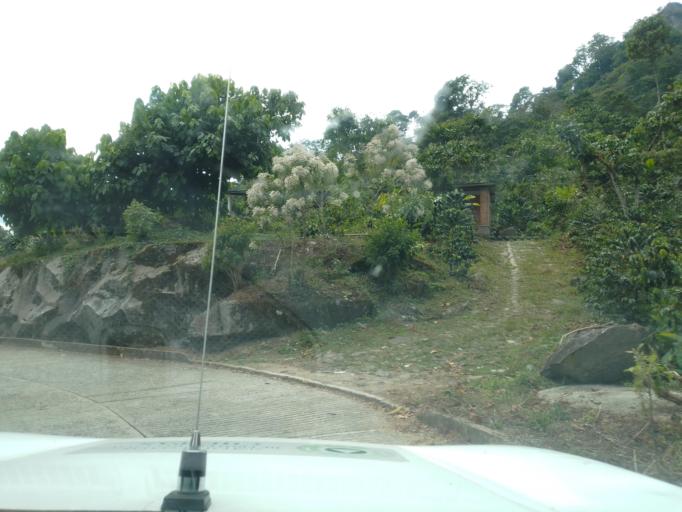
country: MX
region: Chiapas
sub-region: Union Juarez
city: Santo Domingo
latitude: 15.0576
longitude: -92.0928
